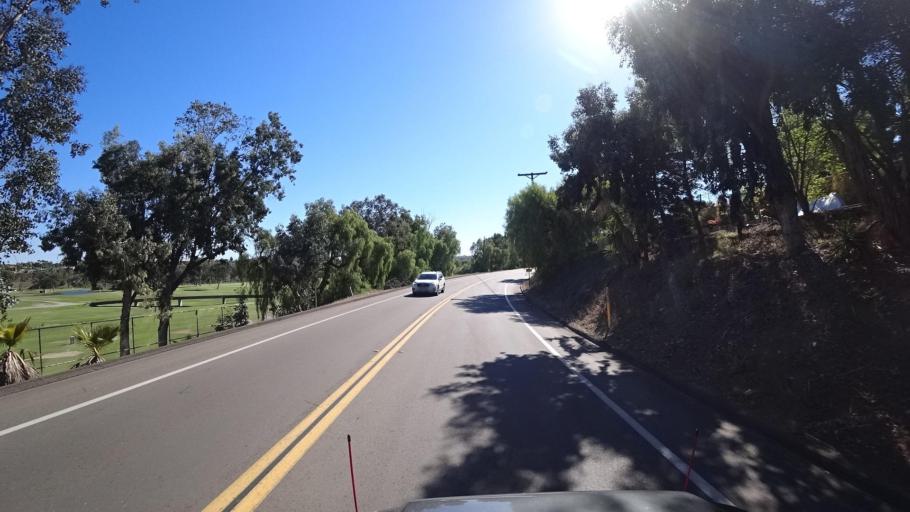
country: US
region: California
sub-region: San Diego County
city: Bonita
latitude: 32.6817
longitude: -117.0141
